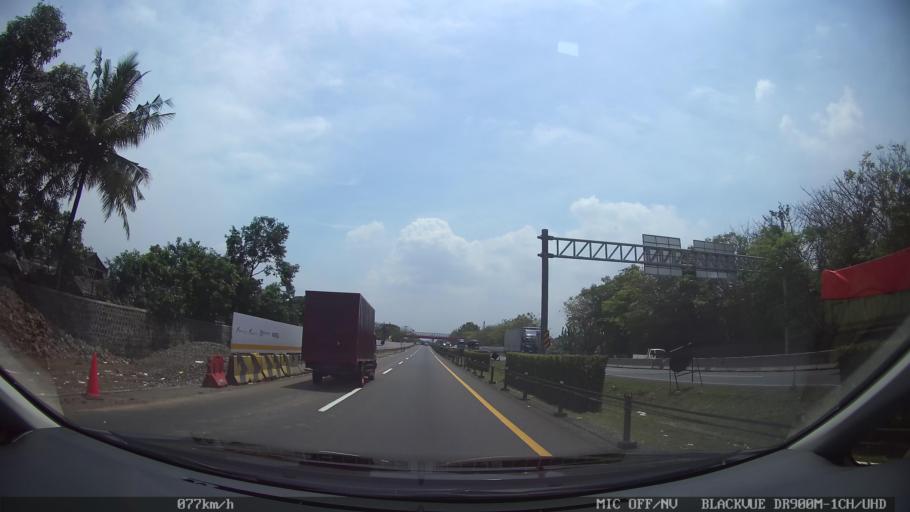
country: ID
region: Banten
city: Serang
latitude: -6.1385
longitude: 106.2334
